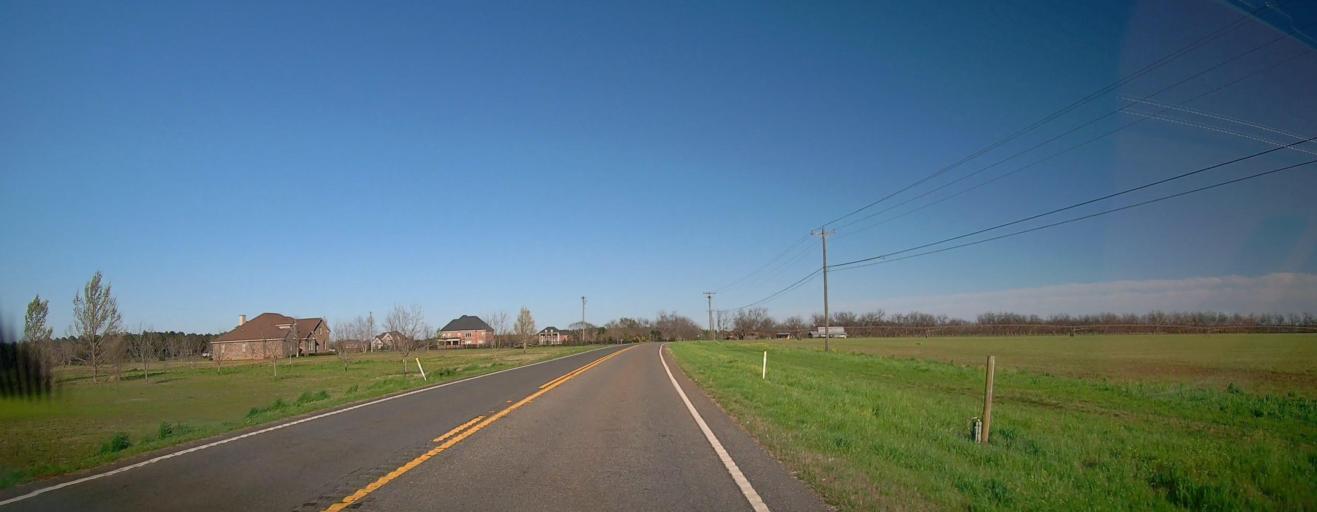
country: US
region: Georgia
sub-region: Houston County
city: Perry
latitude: 32.4407
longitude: -83.8097
